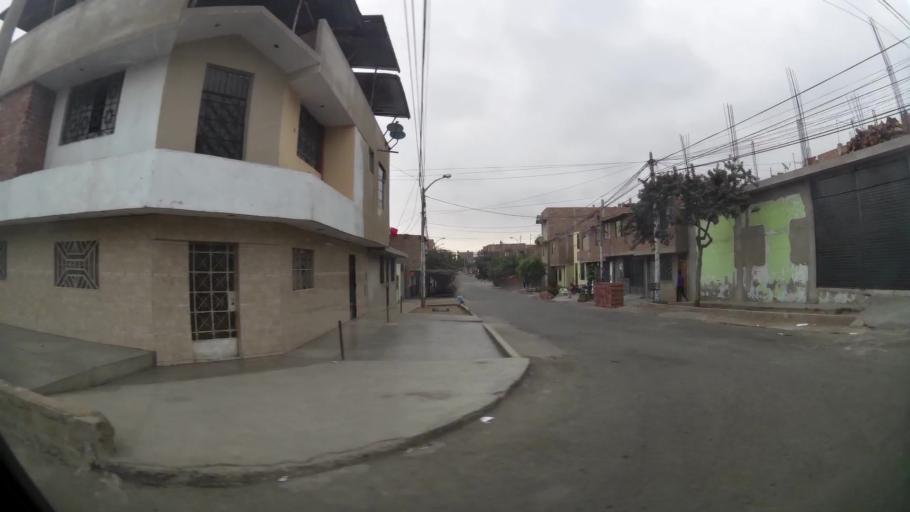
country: PE
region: La Libertad
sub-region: Provincia de Trujillo
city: El Porvenir
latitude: -8.0801
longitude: -79.0197
